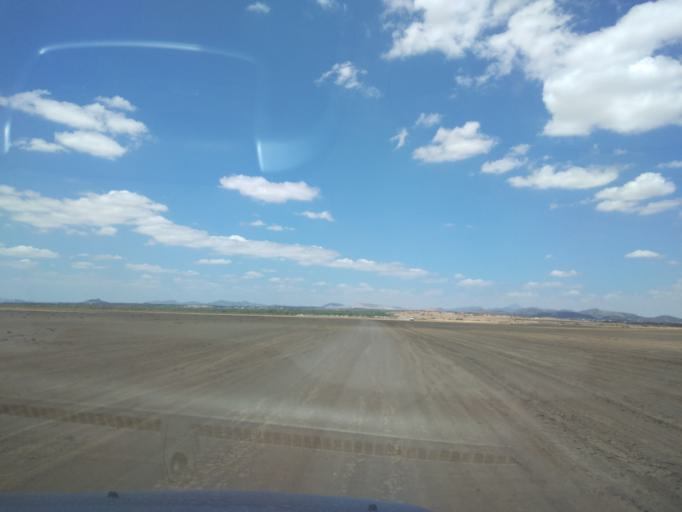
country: TN
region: Susah
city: Harqalah
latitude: 36.1627
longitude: 10.4543
